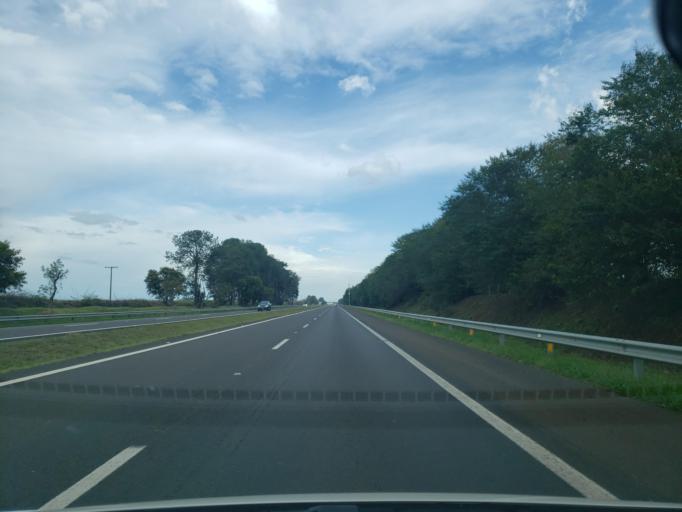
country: BR
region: Sao Paulo
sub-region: Itirapina
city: Itirapina
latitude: -22.2657
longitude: -47.9177
